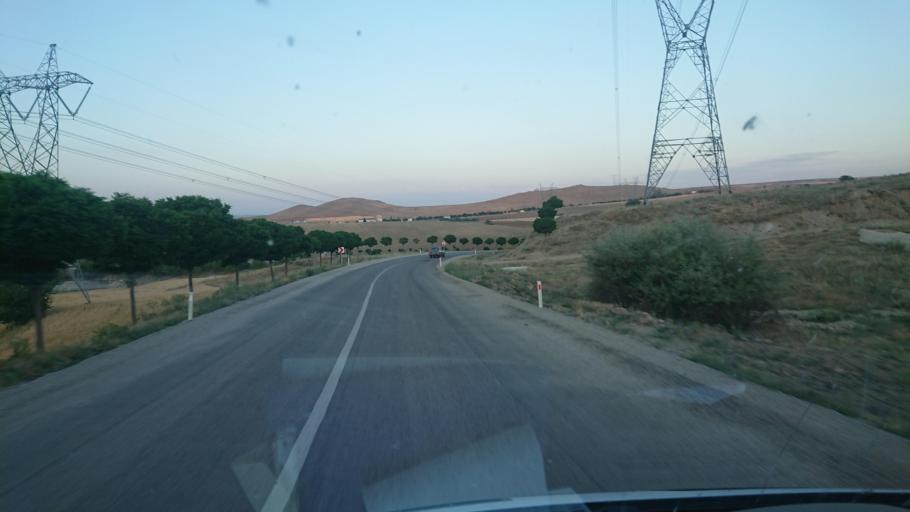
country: TR
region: Aksaray
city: Sariyahsi
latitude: 38.9704
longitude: 33.8240
